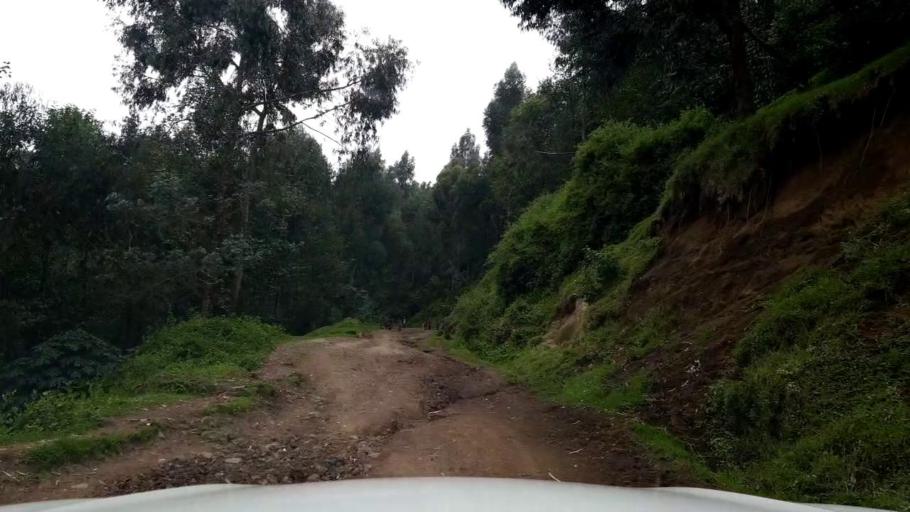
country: RW
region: Western Province
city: Gisenyi
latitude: -1.6518
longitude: 29.4159
